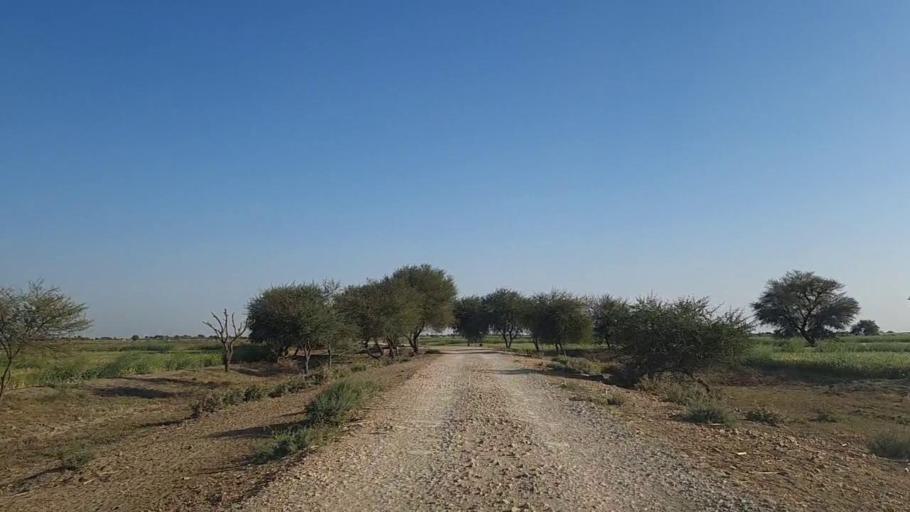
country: PK
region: Sindh
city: Naukot
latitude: 24.9783
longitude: 69.3785
